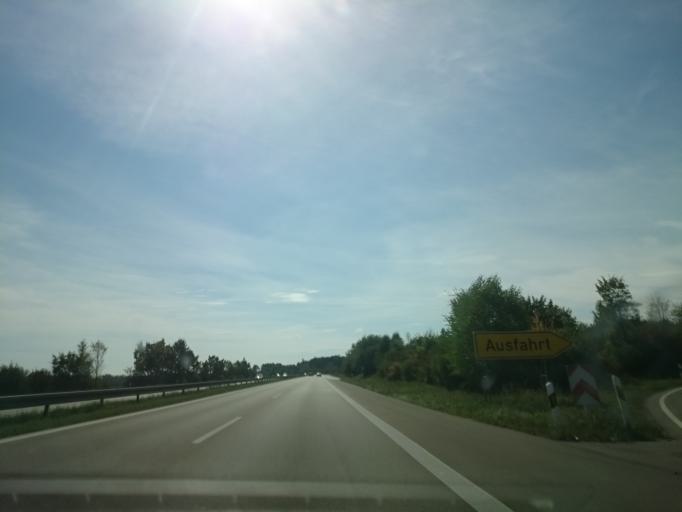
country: DE
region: Bavaria
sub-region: Swabia
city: Langweid
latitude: 48.4847
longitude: 10.8626
